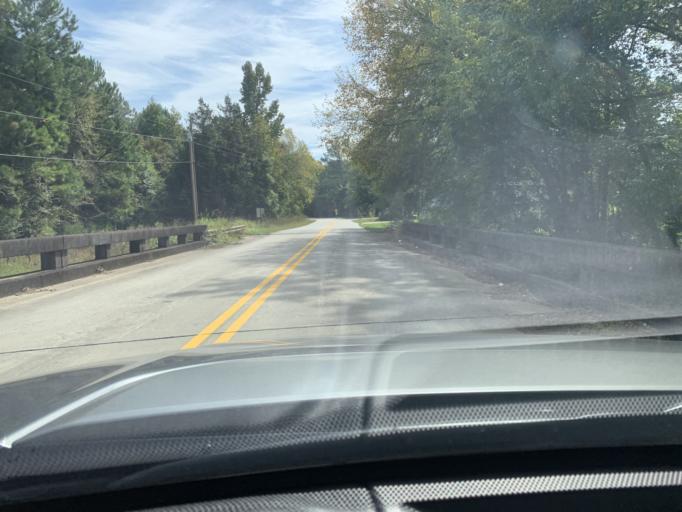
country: US
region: Georgia
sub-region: Polk County
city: Cedartown
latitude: 33.9721
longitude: -85.2699
